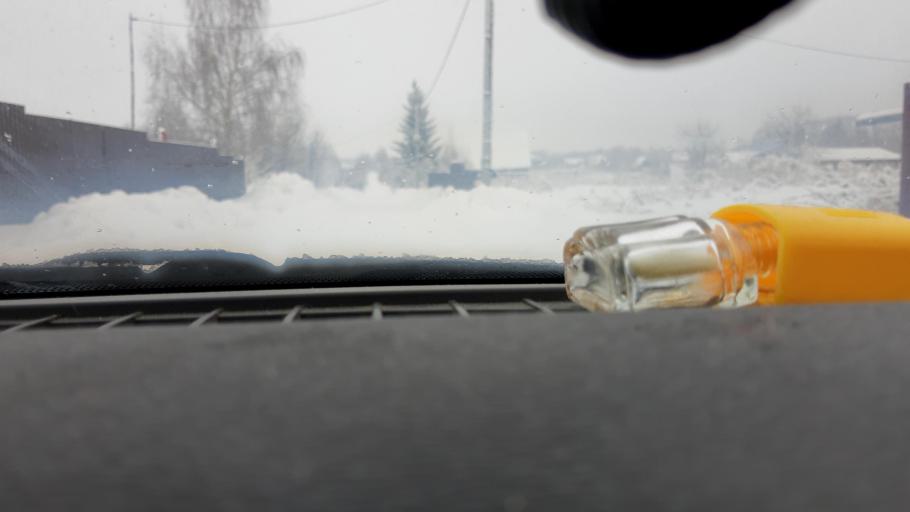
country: RU
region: Bashkortostan
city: Iglino
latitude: 54.7305
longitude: 56.2315
